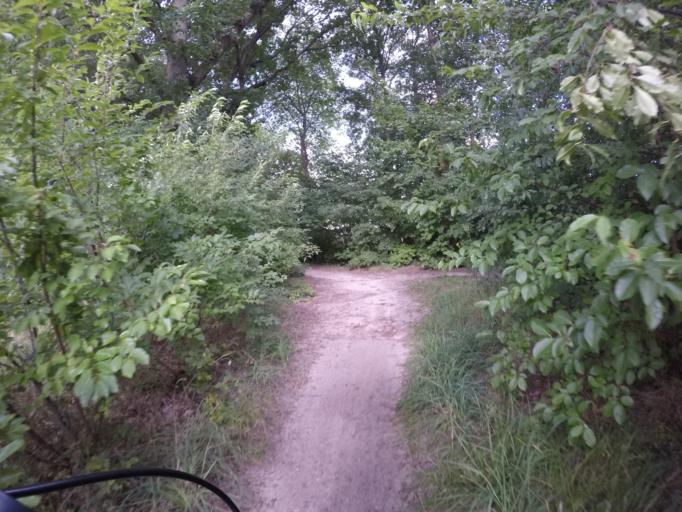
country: DE
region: Brandenburg
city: Werder
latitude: 52.3553
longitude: 12.9816
